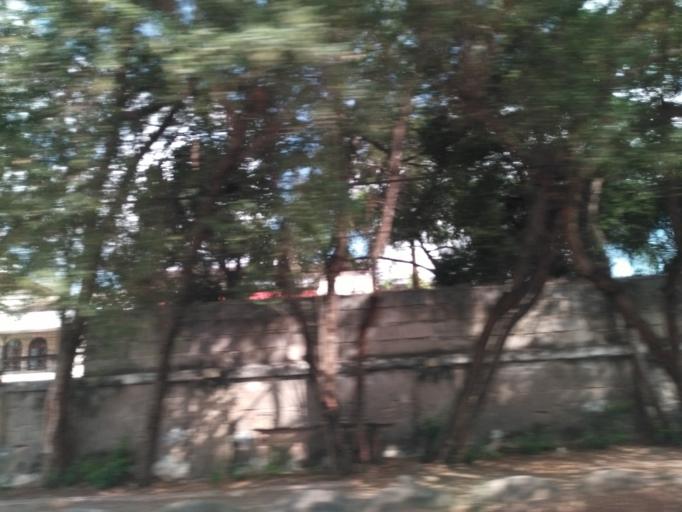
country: TZ
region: Dar es Salaam
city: Magomeni
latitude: -6.7572
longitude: 39.2454
